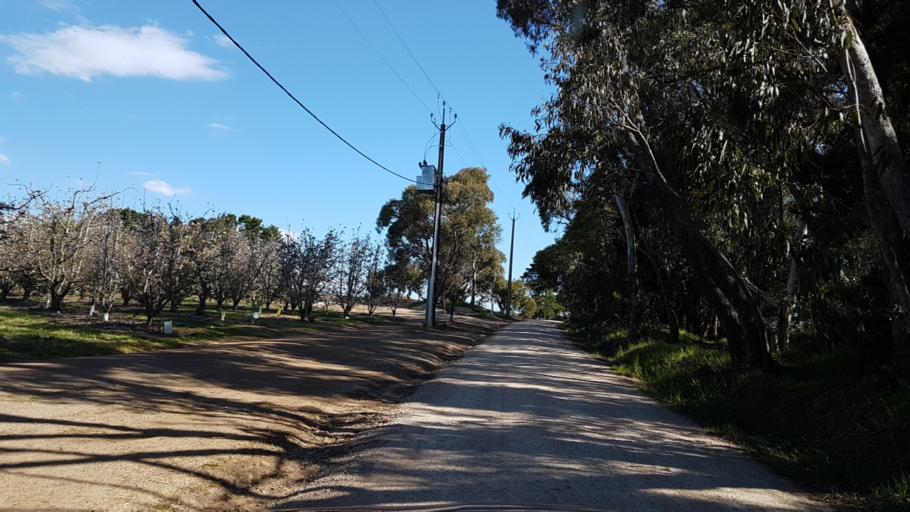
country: AU
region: South Australia
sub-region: Tea Tree Gully
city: Hope Valley
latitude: -34.8483
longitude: 138.7671
